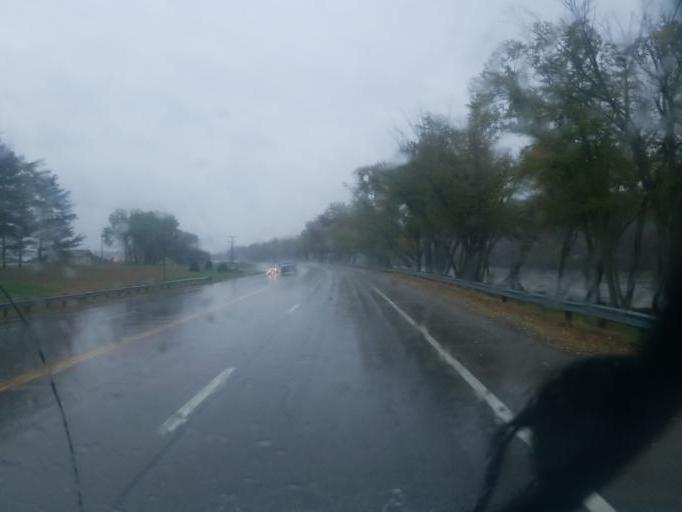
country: US
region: Ohio
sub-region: Muskingum County
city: South Zanesville
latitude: 39.8722
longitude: -81.9542
